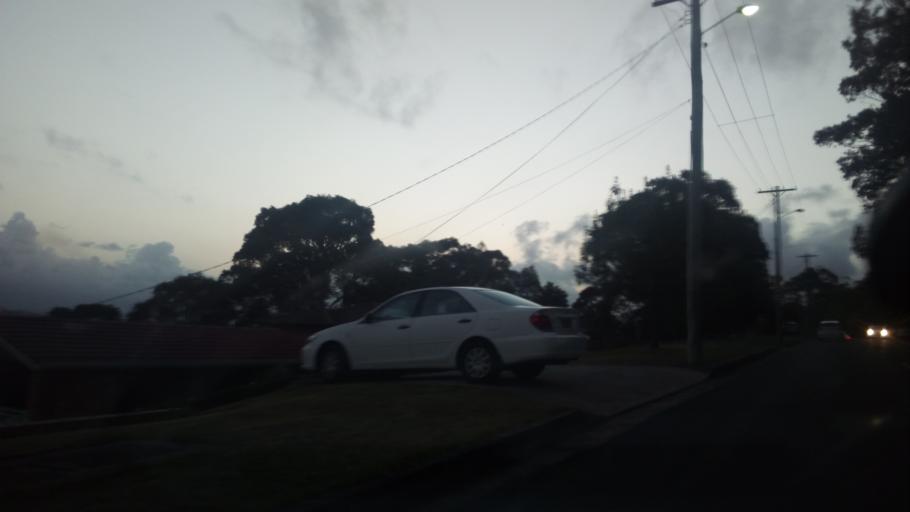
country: AU
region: New South Wales
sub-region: Wollongong
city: Mount Saint Thomas
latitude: -34.4402
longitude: 150.8761
